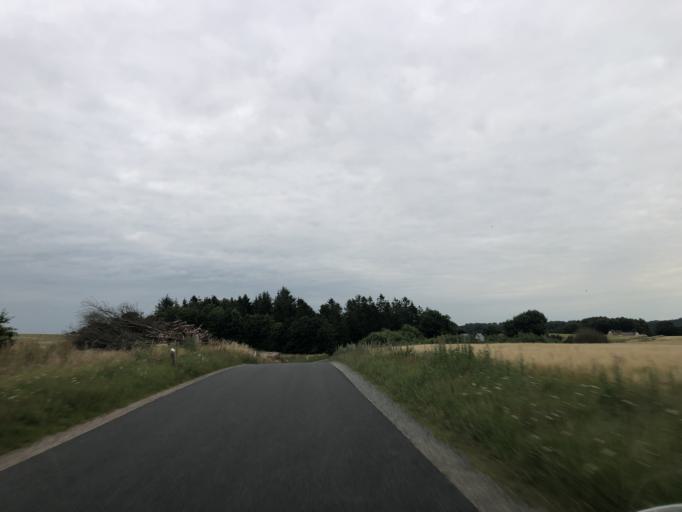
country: DK
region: South Denmark
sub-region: Vejle Kommune
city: Jelling
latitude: 55.7289
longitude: 9.4089
